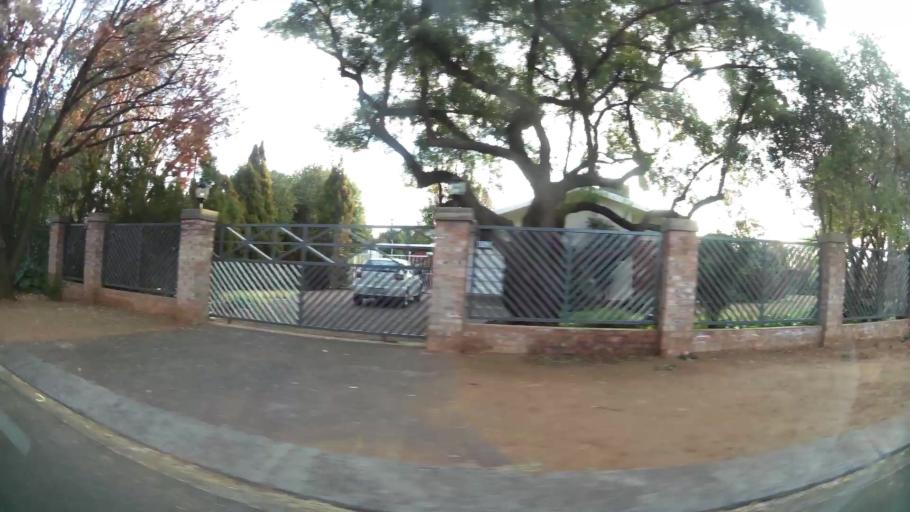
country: ZA
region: Orange Free State
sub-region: Mangaung Metropolitan Municipality
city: Bloemfontein
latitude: -29.1470
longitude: 26.1749
